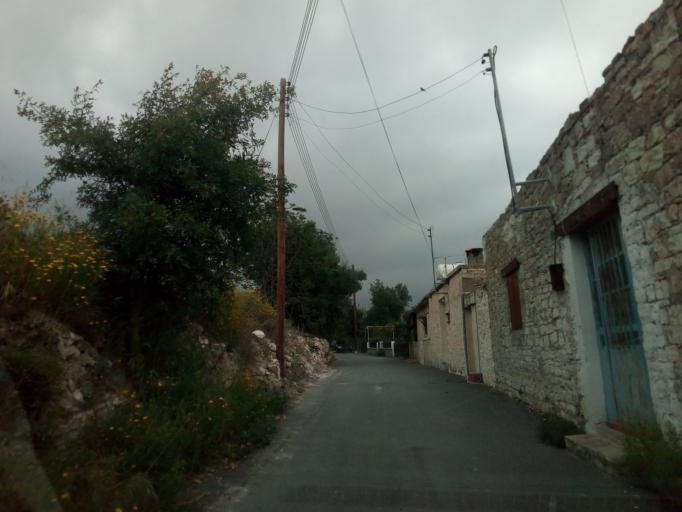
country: CY
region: Pafos
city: Mesogi
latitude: 34.8271
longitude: 32.6154
